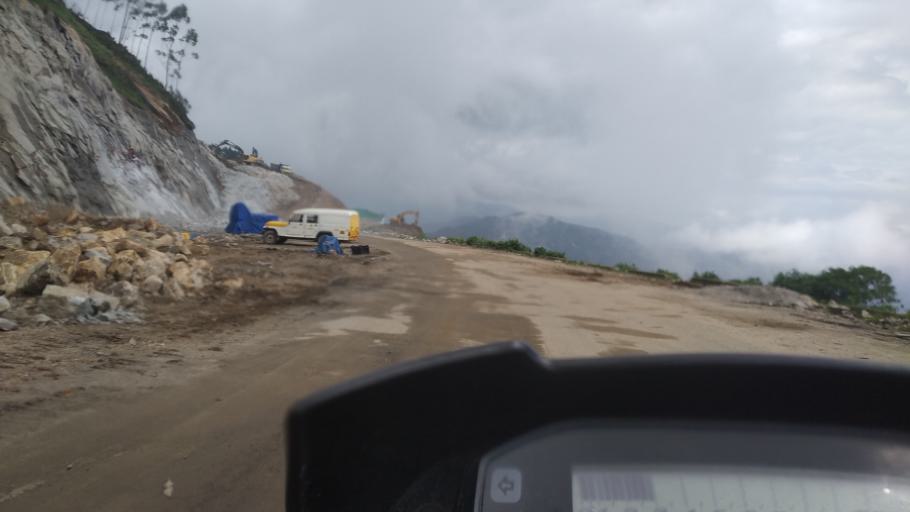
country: IN
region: Kerala
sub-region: Idukki
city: Munnar
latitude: 10.0364
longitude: 77.1353
